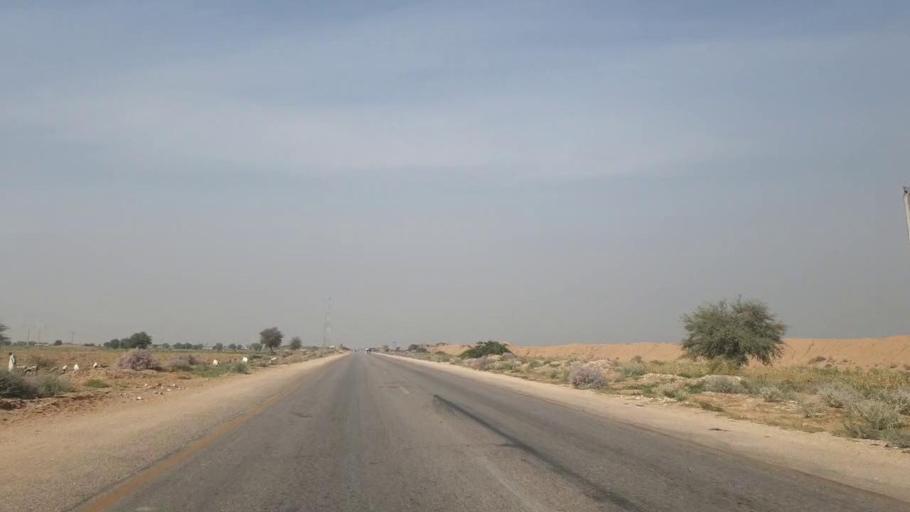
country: PK
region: Sindh
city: Sann
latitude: 26.0445
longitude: 68.1111
